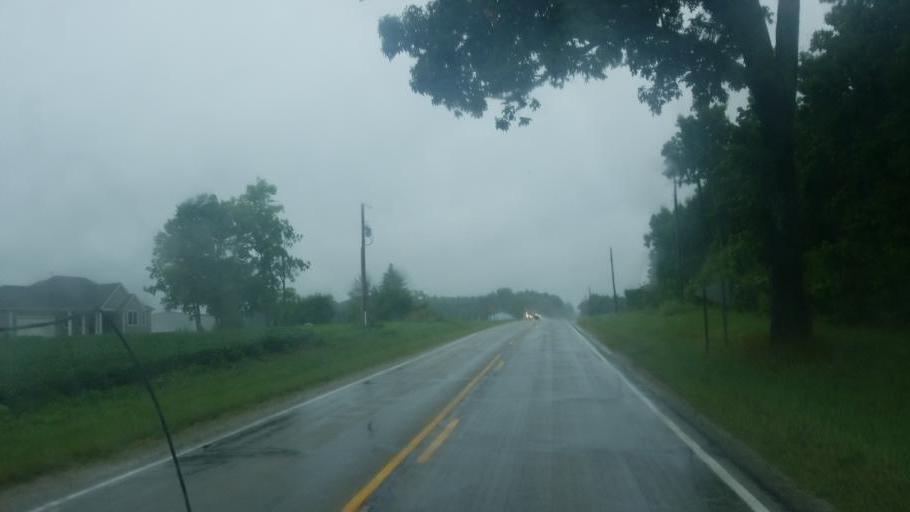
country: US
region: Indiana
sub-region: Huntington County
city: Warren
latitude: 40.6587
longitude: -85.4021
